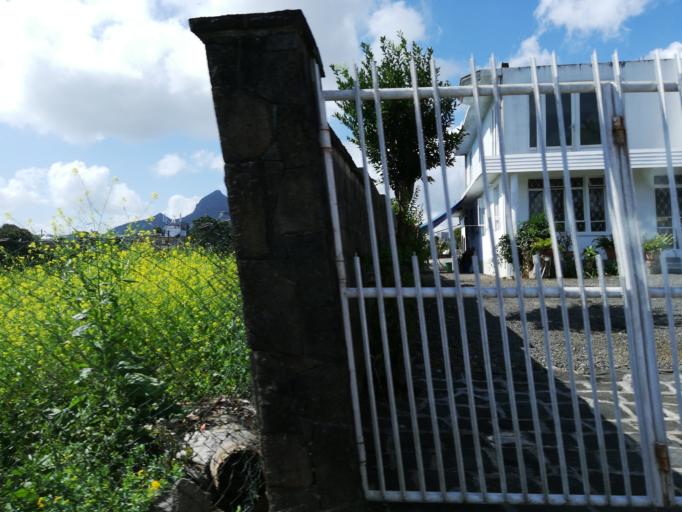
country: MU
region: Moka
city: Verdun
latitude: -20.2182
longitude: 57.5384
